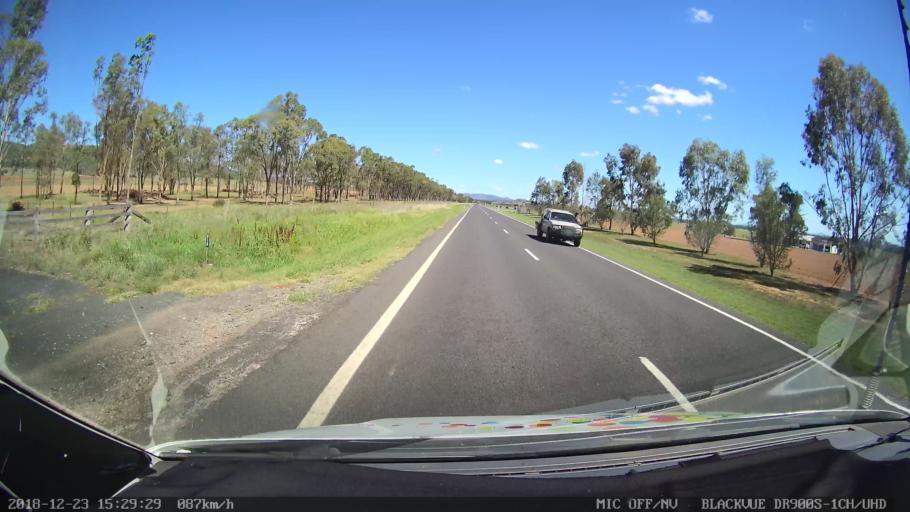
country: AU
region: New South Wales
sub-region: Tamworth Municipality
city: East Tamworth
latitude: -30.9473
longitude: 150.8609
